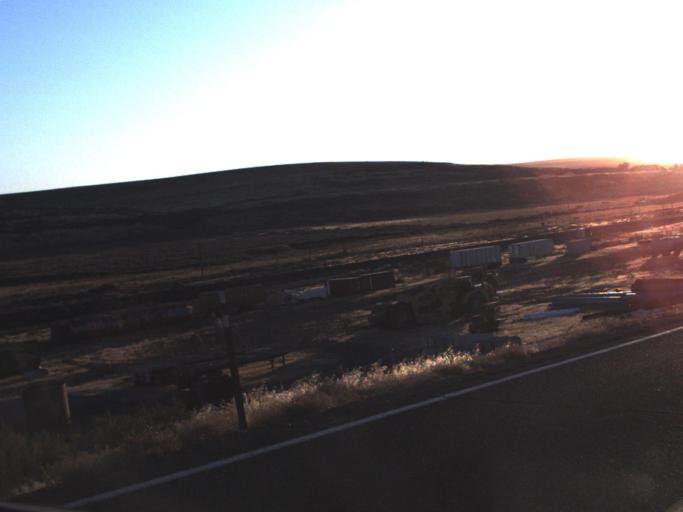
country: US
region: Washington
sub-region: Adams County
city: Ritzville
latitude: 46.9698
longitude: -118.5829
